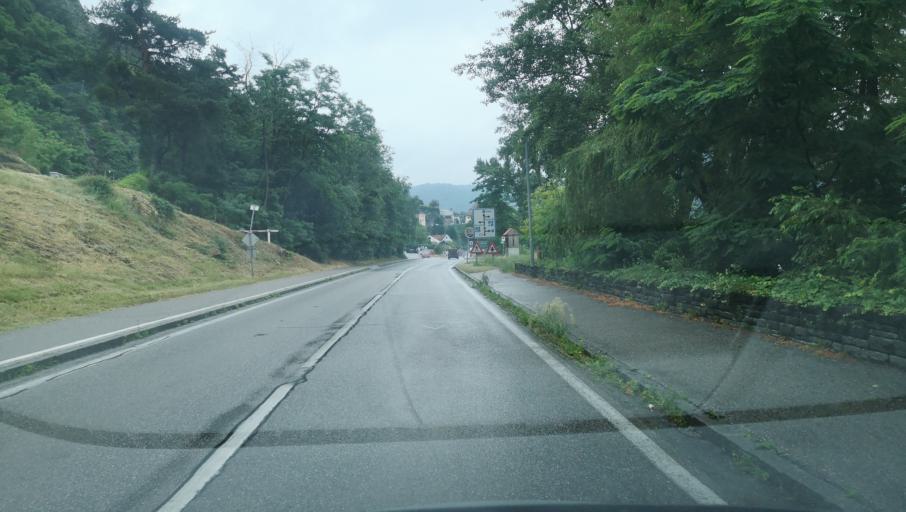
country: AT
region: Lower Austria
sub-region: Politischer Bezirk Krems
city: Durnstein
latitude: 48.4009
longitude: 15.5173
